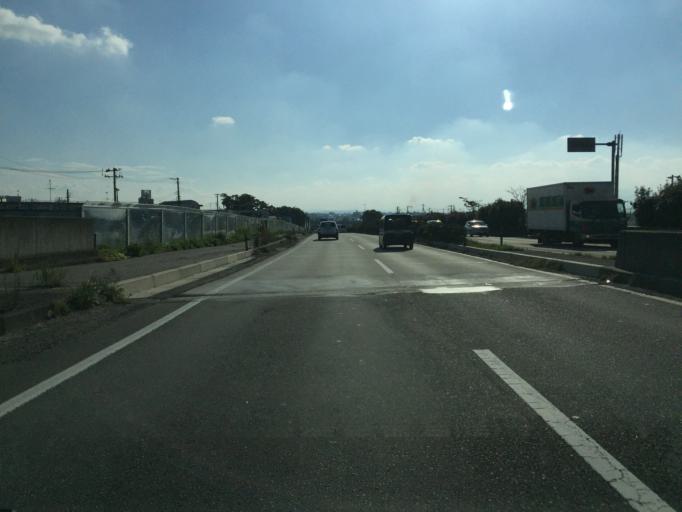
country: JP
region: Fukushima
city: Koriyama
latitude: 37.4262
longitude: 140.3596
